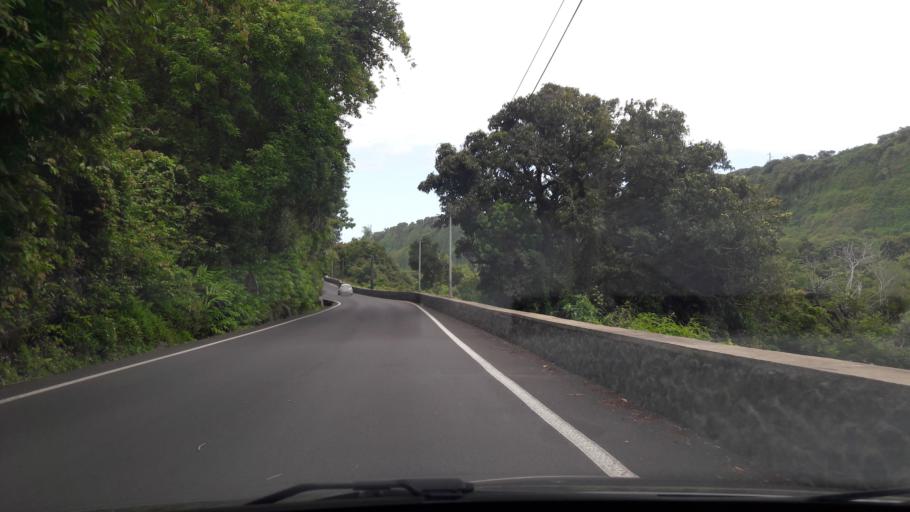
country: RE
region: Reunion
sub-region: Reunion
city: Saint-Andre
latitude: -20.9867
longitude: 55.6222
